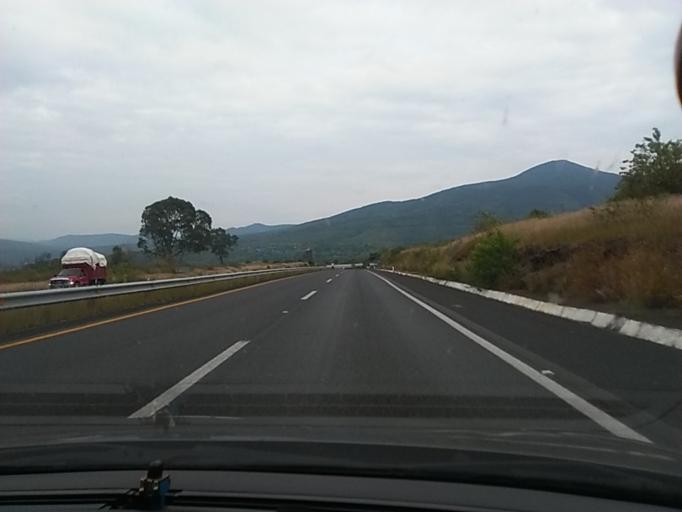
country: MX
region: Michoacan
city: Panindicuaro de la Reforma
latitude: 19.9742
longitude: -101.7688
